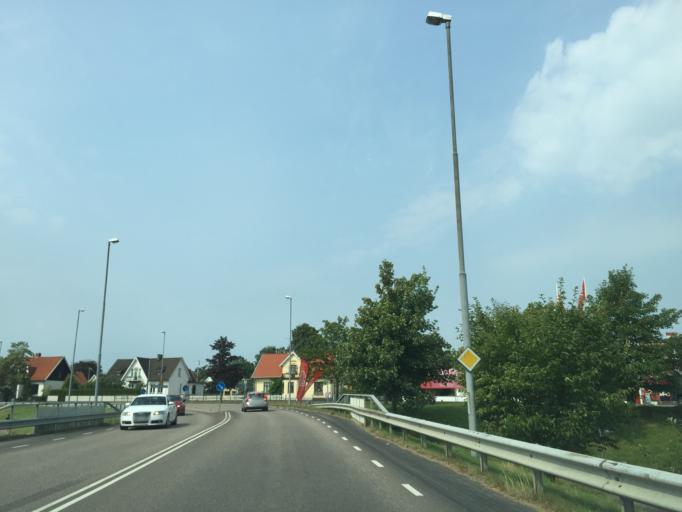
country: SE
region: Skane
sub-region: Angelholms Kommun
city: AEngelholm
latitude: 56.2355
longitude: 12.8583
